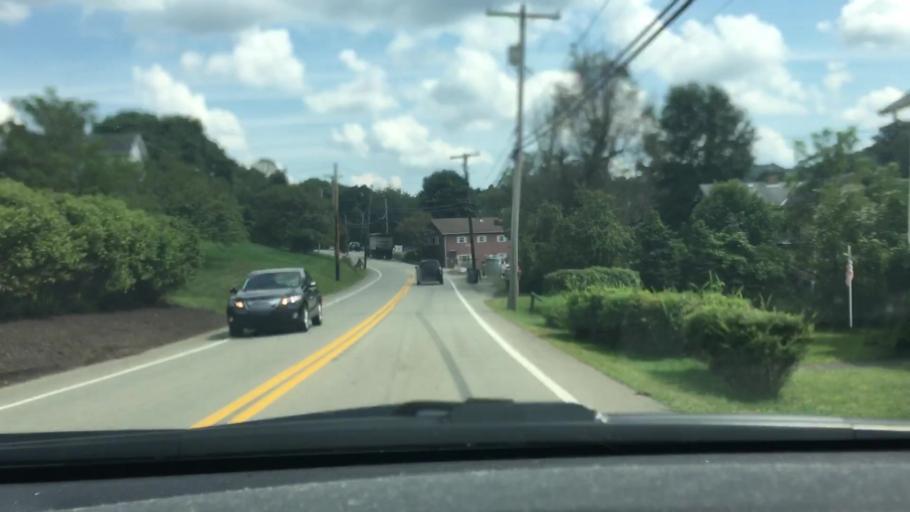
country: US
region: Pennsylvania
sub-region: Washington County
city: Gastonville
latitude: 40.2462
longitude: -80.0391
